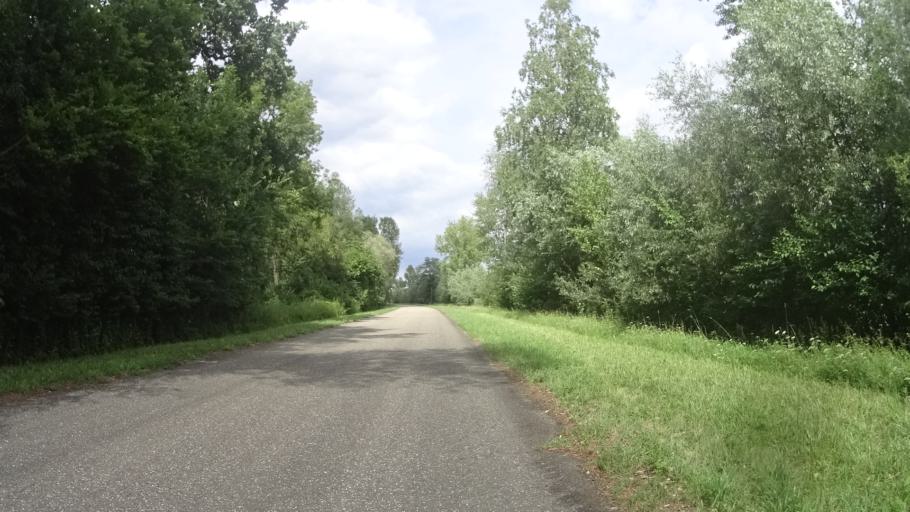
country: DE
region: Baden-Wuerttemberg
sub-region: Karlsruhe Region
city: Rheinmuenster
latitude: 48.7642
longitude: 8.0160
